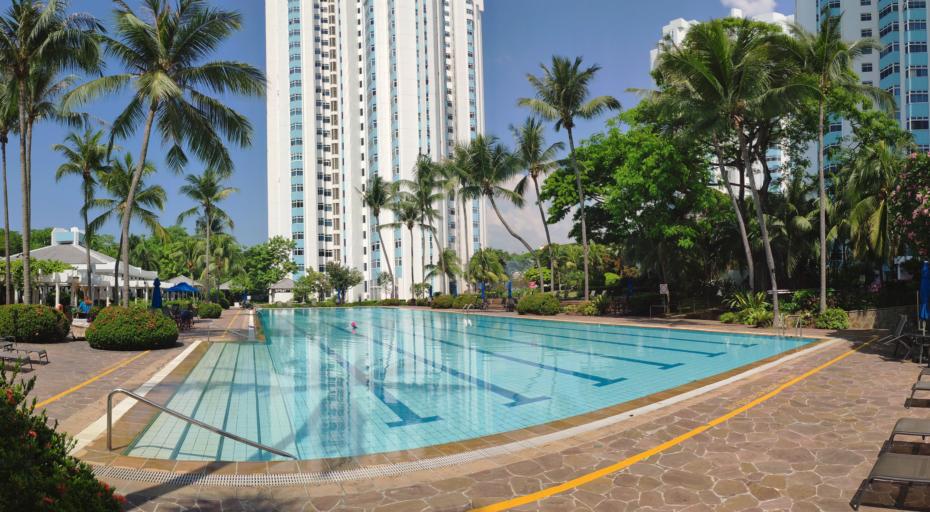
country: SG
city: Singapore
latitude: 1.2971
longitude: 103.8836
